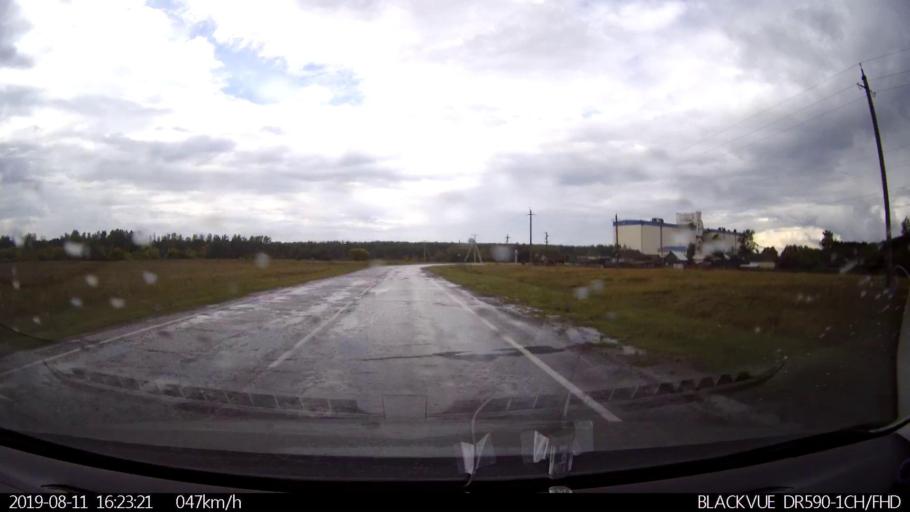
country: RU
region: Ulyanovsk
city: Mayna
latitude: 54.0946
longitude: 47.5888
